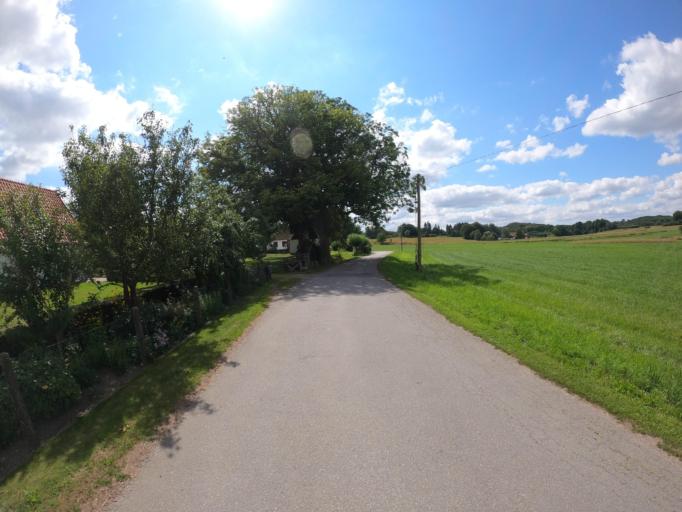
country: SE
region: Skane
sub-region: Lunds Kommun
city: Veberod
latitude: 55.5924
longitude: 13.4969
